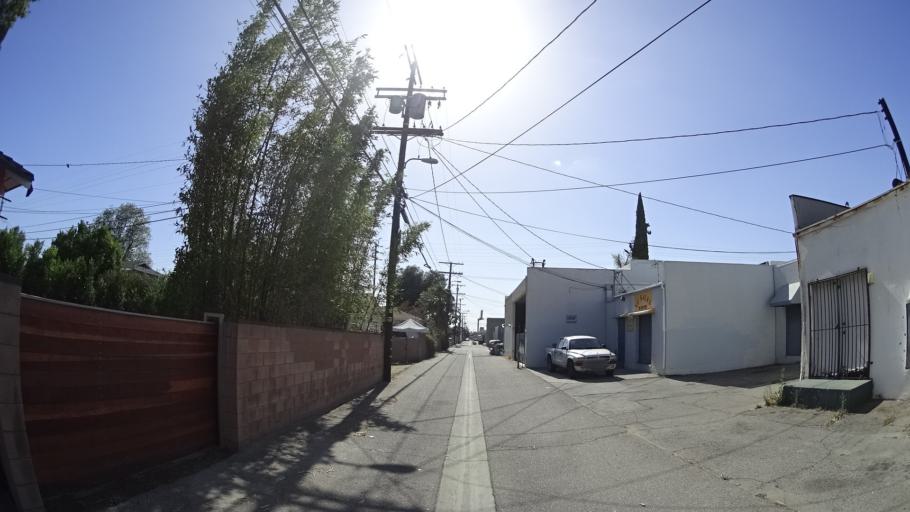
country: US
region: California
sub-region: Los Angeles County
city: North Hollywood
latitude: 34.1717
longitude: -118.3597
